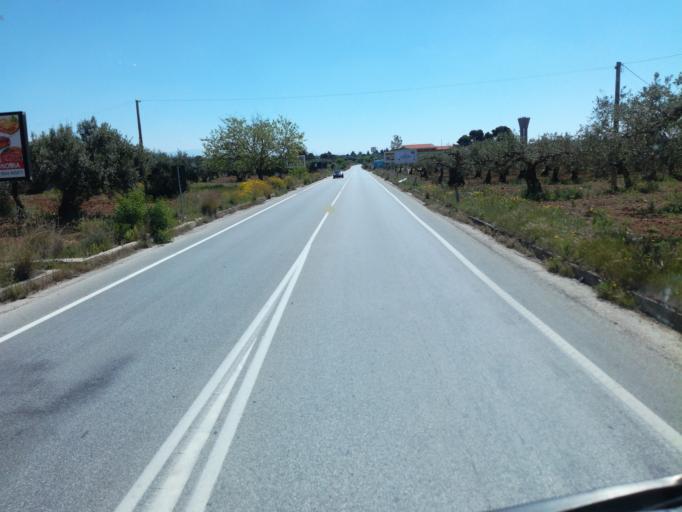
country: IT
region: Sicily
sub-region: Trapani
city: Castelvetrano
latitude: 37.6580
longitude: 12.8154
